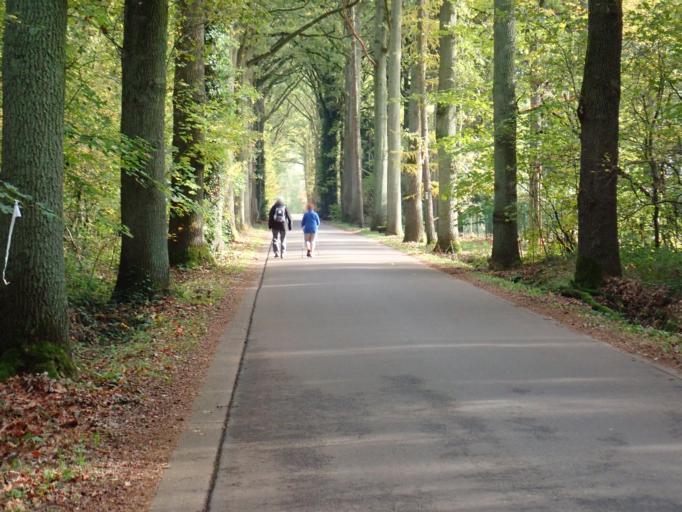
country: BE
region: Flanders
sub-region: Provincie Antwerpen
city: Zoersel
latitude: 51.2568
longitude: 4.7053
